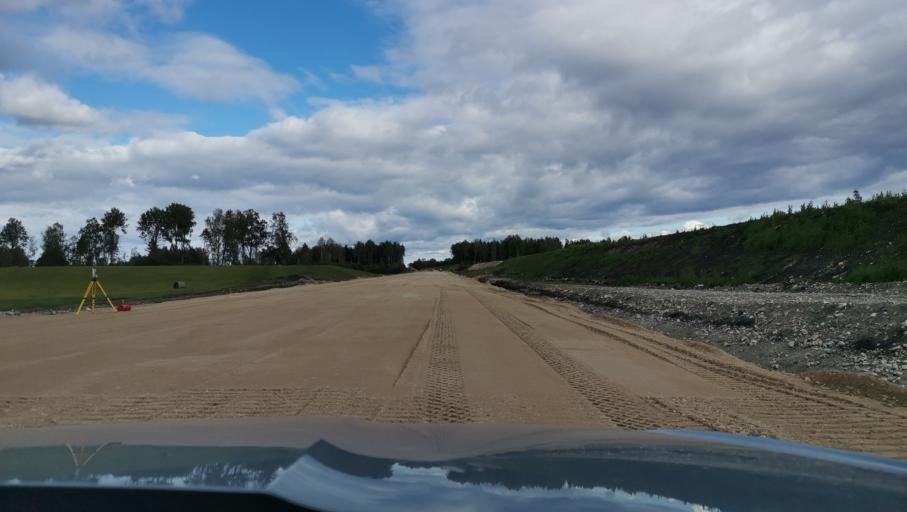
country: EE
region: Harju
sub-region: Keila linn
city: Keila
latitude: 59.1438
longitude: 24.4947
